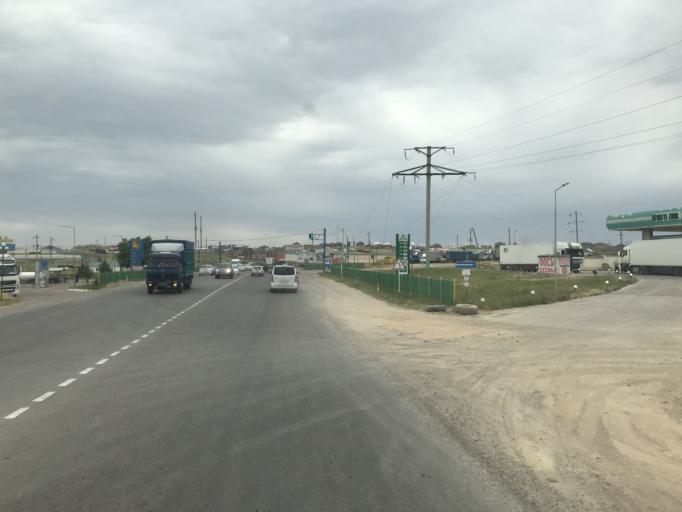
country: KZ
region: Ongtustik Qazaqstan
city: Saryaghash
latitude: 41.4761
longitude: 69.2079
